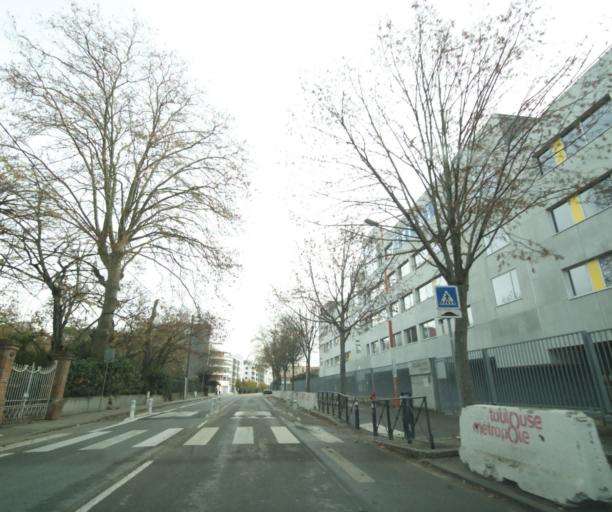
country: FR
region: Midi-Pyrenees
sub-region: Departement de la Haute-Garonne
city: Ramonville-Saint-Agne
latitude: 43.5759
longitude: 1.4713
